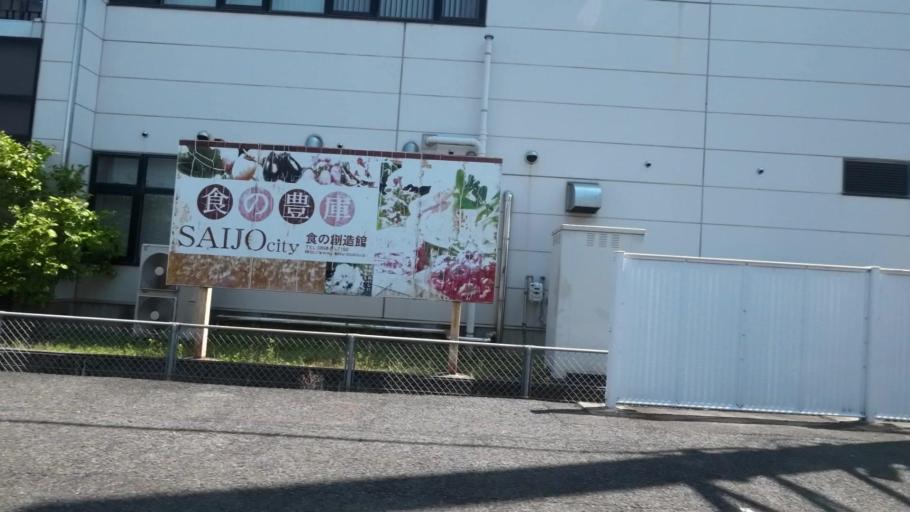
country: JP
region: Ehime
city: Saijo
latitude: 33.9295
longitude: 133.0858
